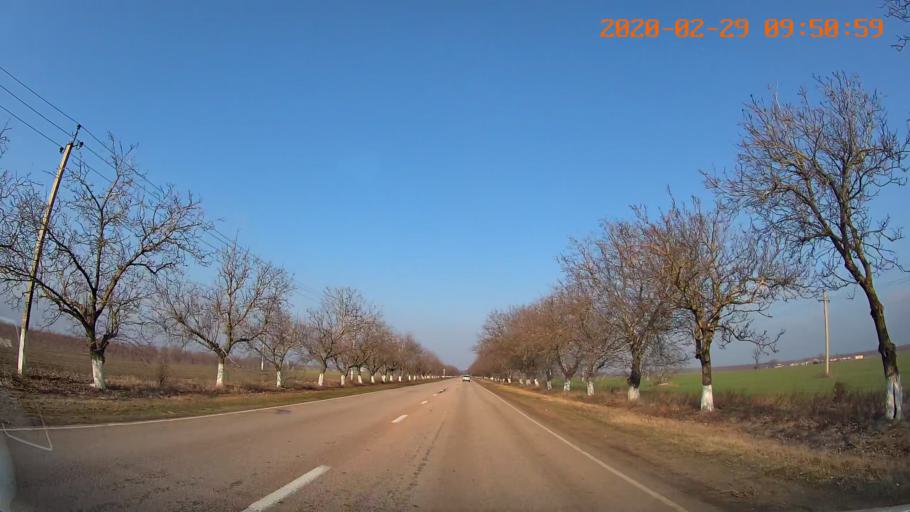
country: MD
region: Telenesti
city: Slobozia
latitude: 46.7050
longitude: 29.7466
